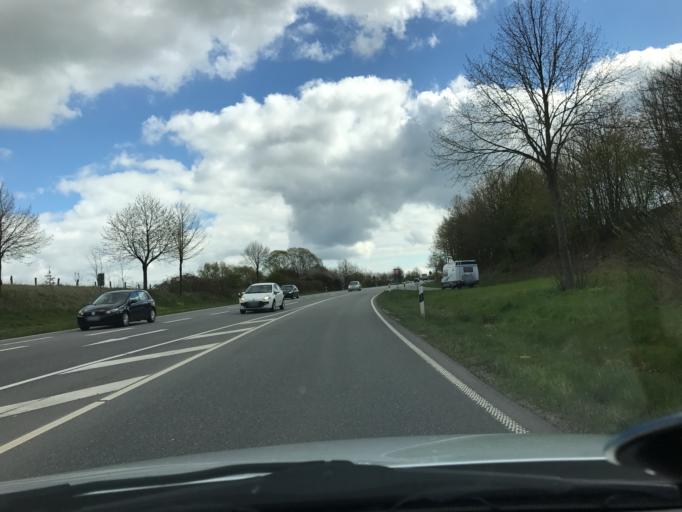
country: DE
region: Schleswig-Holstein
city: Eutin
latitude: 54.1190
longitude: 10.6401
